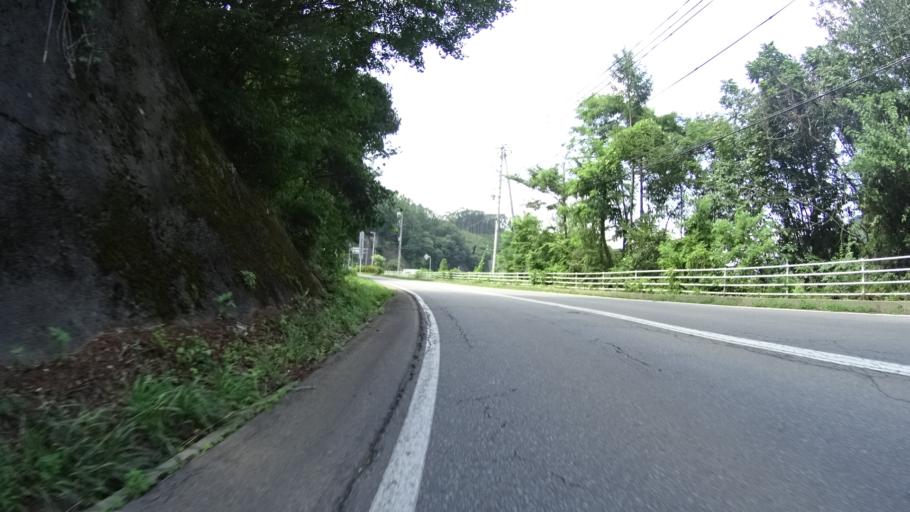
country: JP
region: Nagano
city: Saku
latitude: 36.0818
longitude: 138.4877
